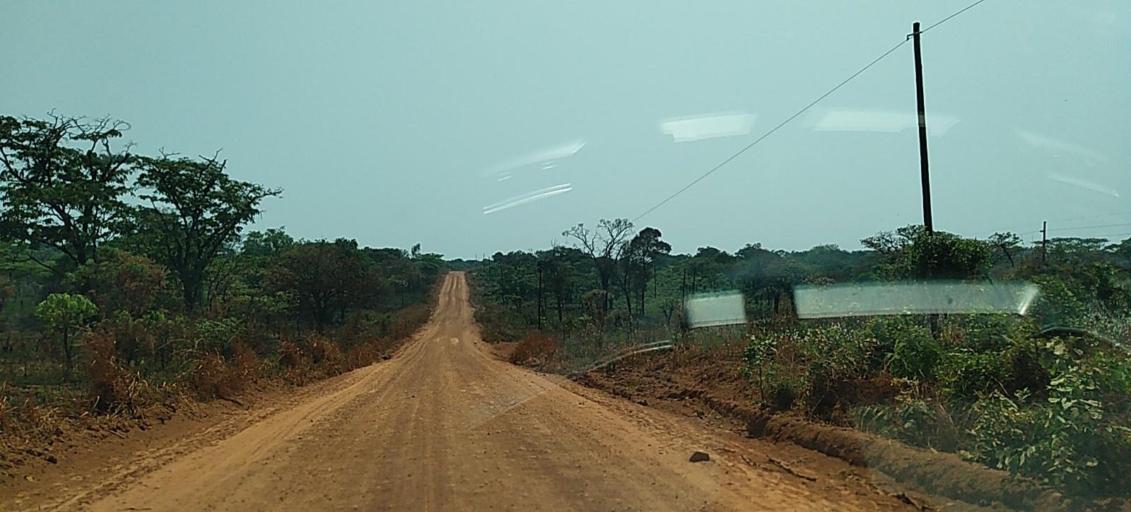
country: ZM
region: North-Western
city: Kansanshi
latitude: -11.9996
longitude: 26.5921
